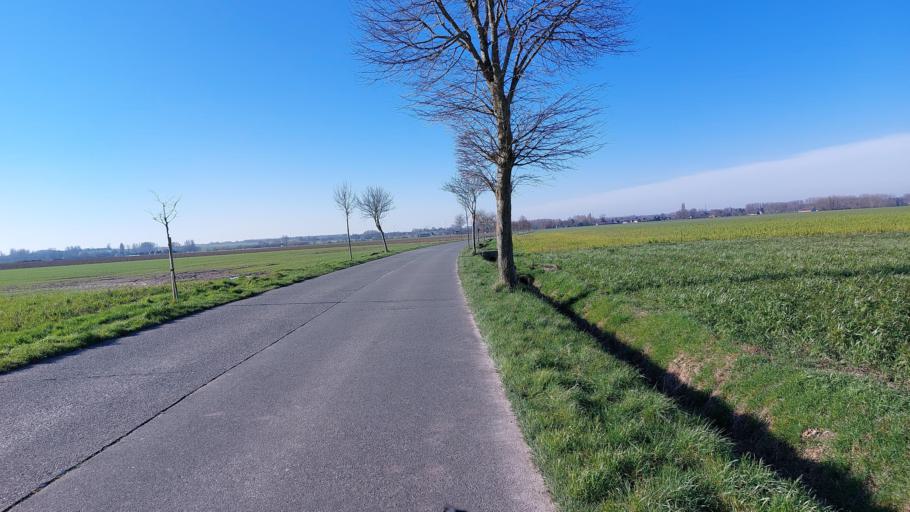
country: BE
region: Wallonia
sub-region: Province du Hainaut
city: Chievres
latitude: 50.5753
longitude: 3.7955
